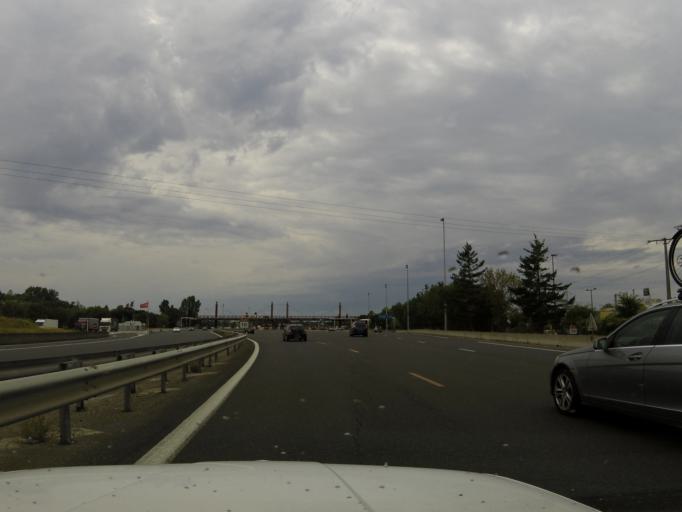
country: FR
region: Rhone-Alpes
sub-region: Departement de l'Ain
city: Beynost
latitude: 45.8222
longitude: 4.9971
